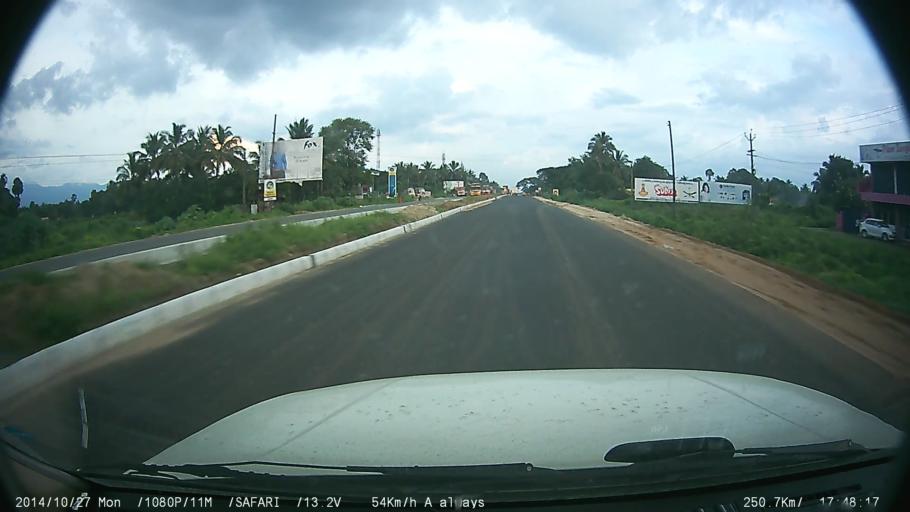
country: IN
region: Kerala
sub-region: Palakkad district
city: Palakkad
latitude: 10.7376
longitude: 76.6318
